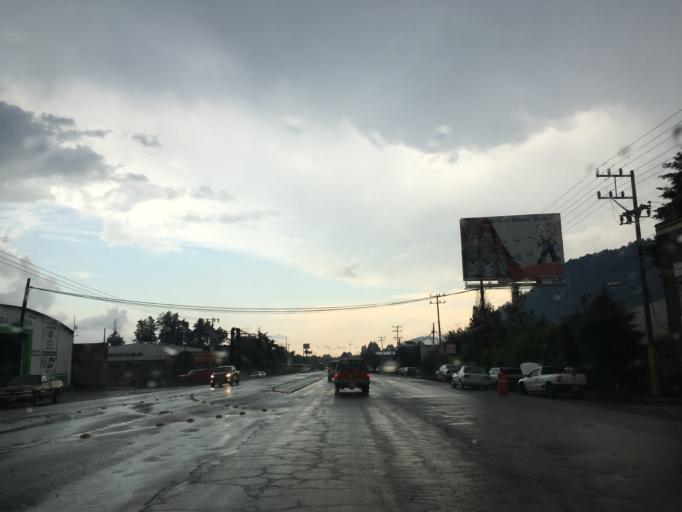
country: MX
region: Michoacan
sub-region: Uruapan
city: Uruapan
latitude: 19.4775
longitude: -102.0712
